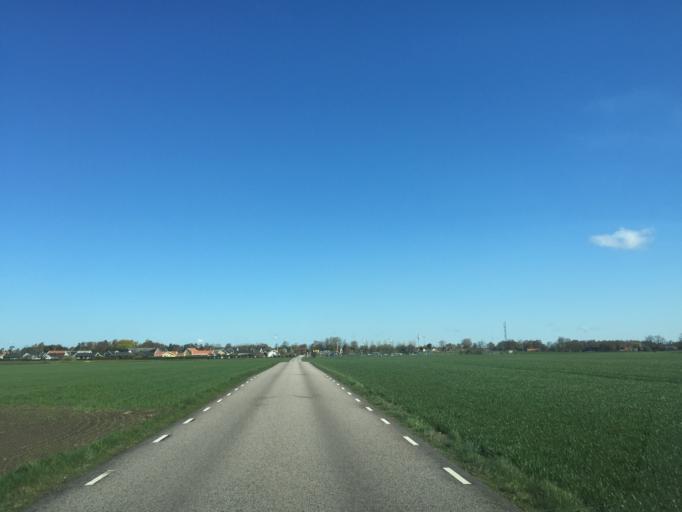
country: SE
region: Skane
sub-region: Kavlinge Kommun
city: Loddekopinge
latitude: 55.8132
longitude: 13.0256
